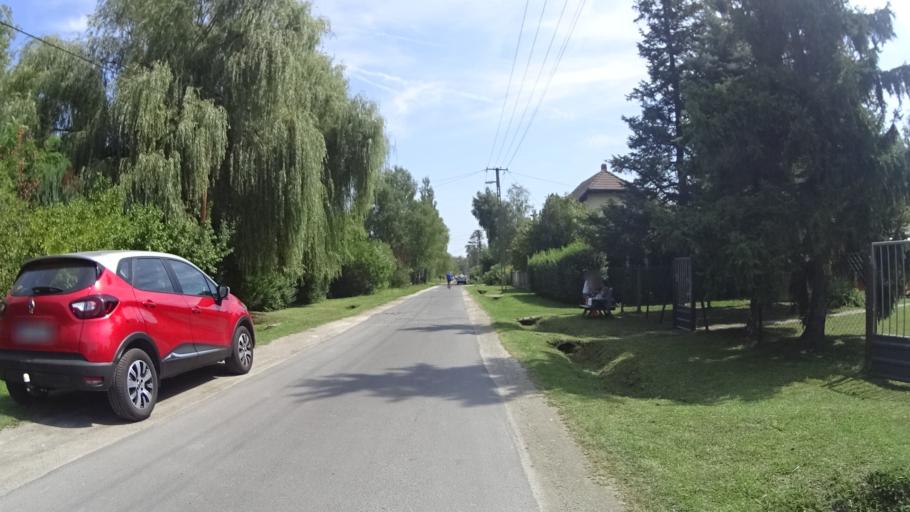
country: HU
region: Somogy
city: Balatonfenyves
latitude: 46.7080
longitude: 17.4481
